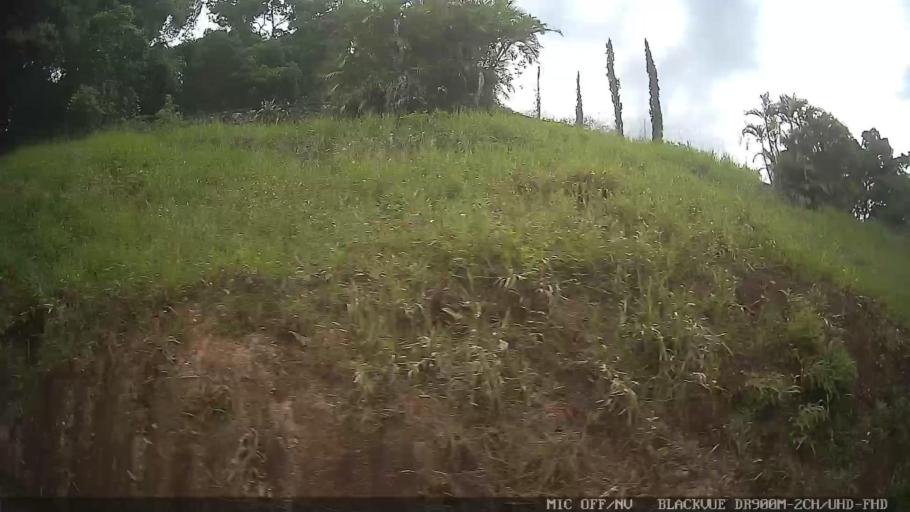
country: BR
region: Sao Paulo
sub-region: Atibaia
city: Atibaia
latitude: -23.1554
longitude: -46.5671
